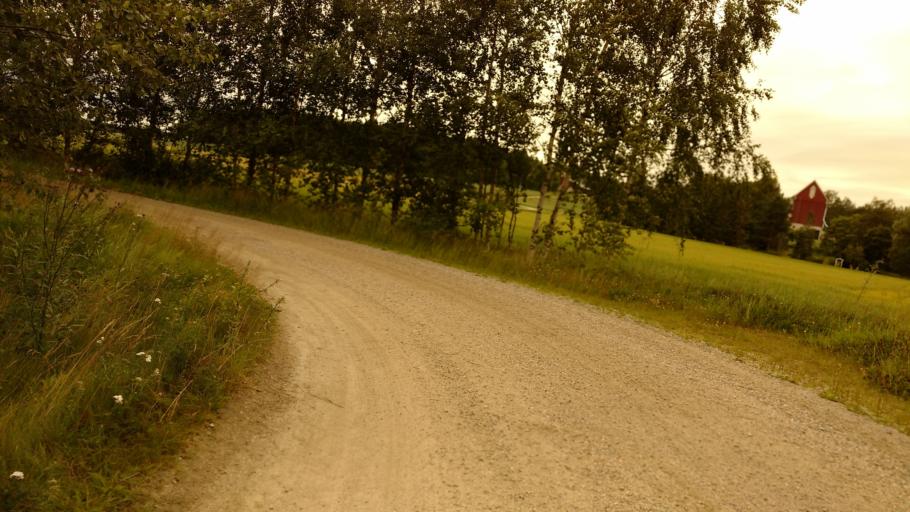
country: FI
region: Varsinais-Suomi
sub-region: Turku
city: Paimio
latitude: 60.4191
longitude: 22.8331
